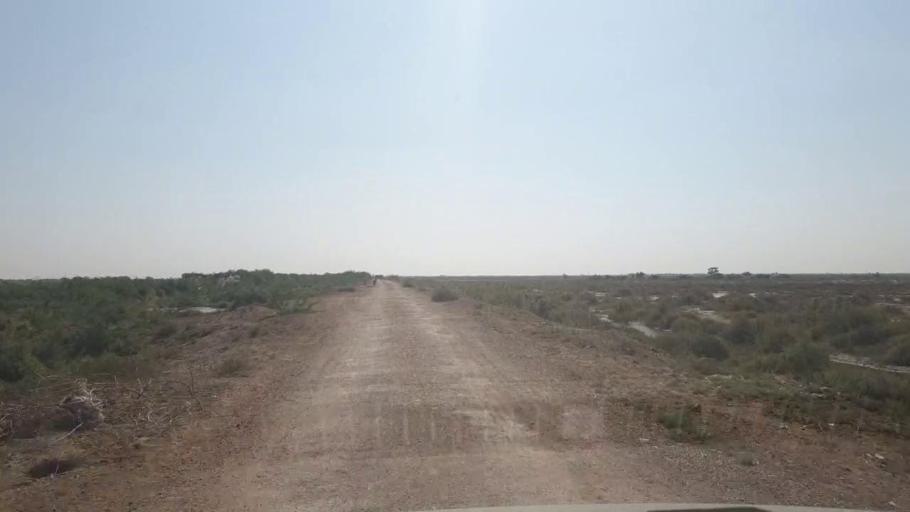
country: PK
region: Sindh
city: Tando Bago
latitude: 24.8768
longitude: 69.1643
